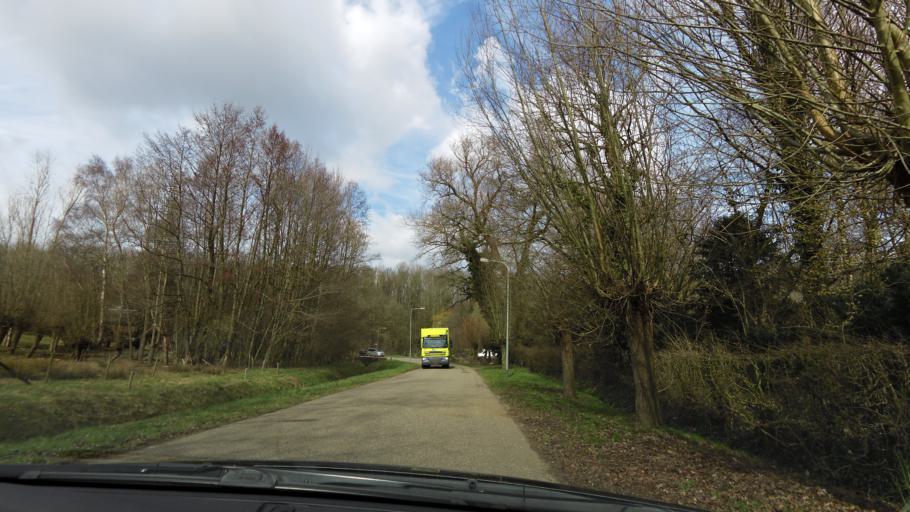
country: NL
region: Limburg
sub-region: Gemeente Simpelveld
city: Simpelveld
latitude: 50.8270
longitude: 5.9987
